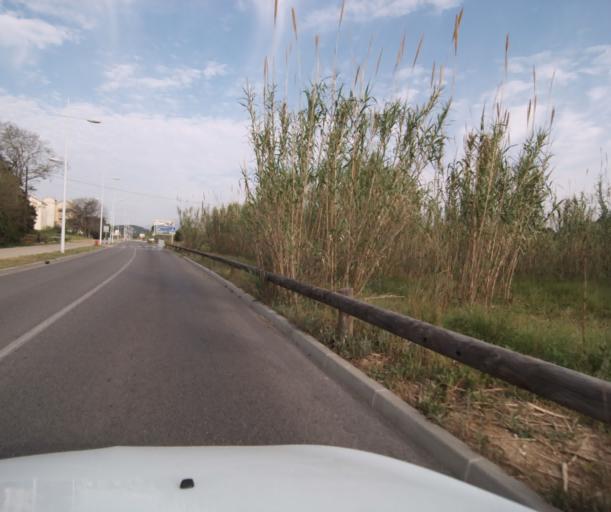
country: FR
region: Provence-Alpes-Cote d'Azur
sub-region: Departement du Var
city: Hyeres
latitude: 43.1122
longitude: 6.1203
